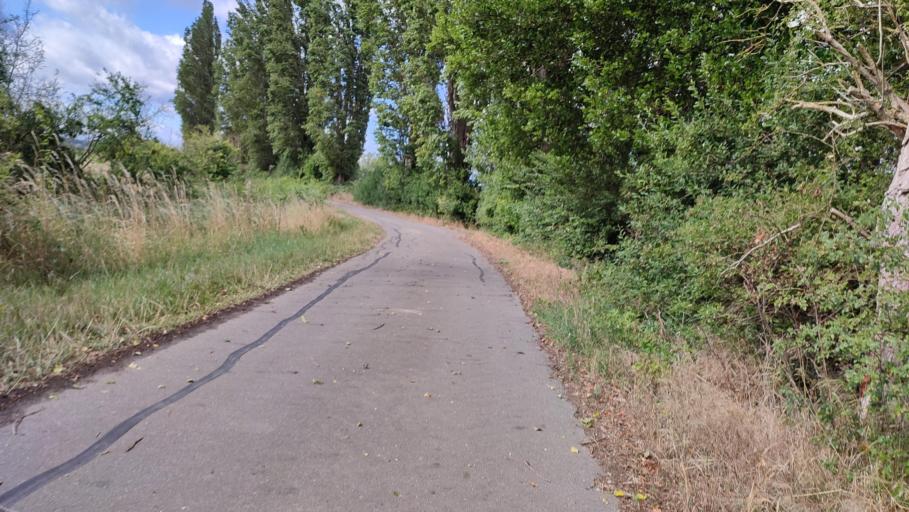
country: DE
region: Lower Saxony
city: Neu Darchau
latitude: 53.2330
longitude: 10.9650
